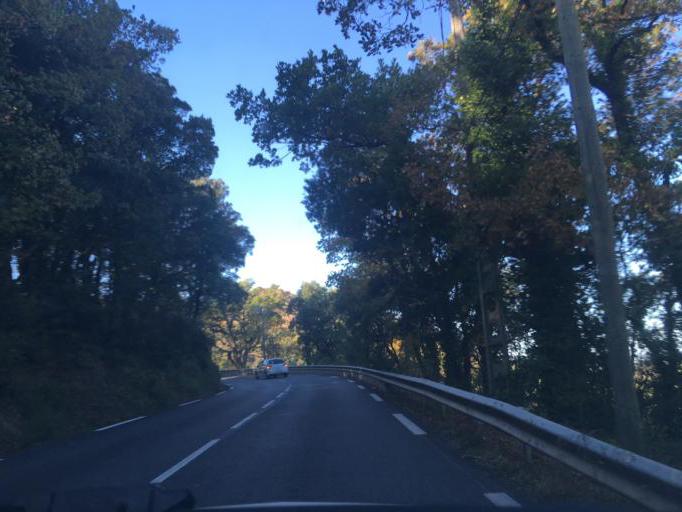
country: FR
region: Provence-Alpes-Cote d'Azur
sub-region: Departement du Var
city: La Garde-Freinet
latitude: 43.3222
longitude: 6.4753
